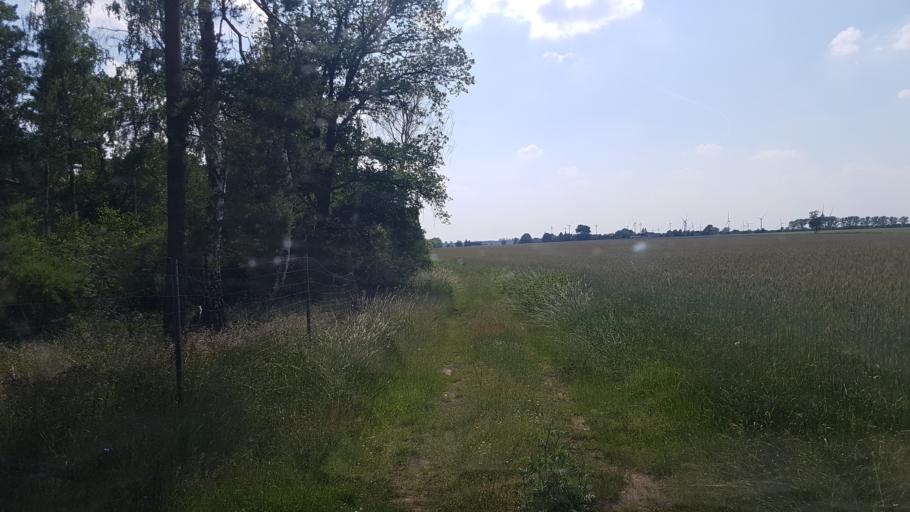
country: DE
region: Brandenburg
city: Trobitz
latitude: 51.6636
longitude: 13.4481
